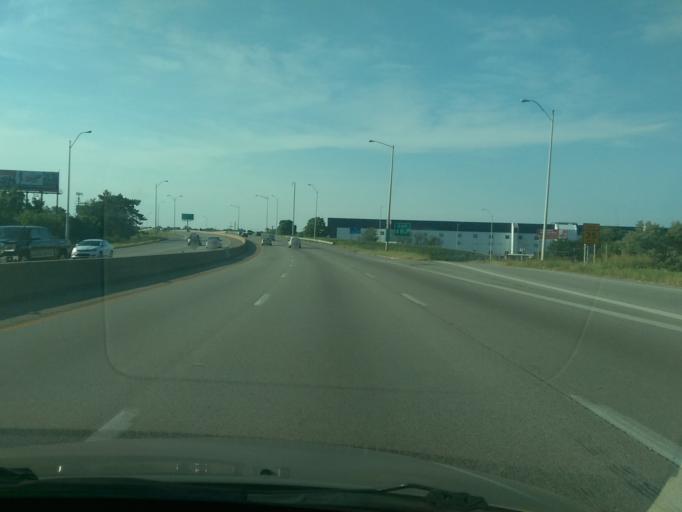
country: US
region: Missouri
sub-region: Jackson County
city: Kansas City
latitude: 39.0872
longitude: -94.5411
